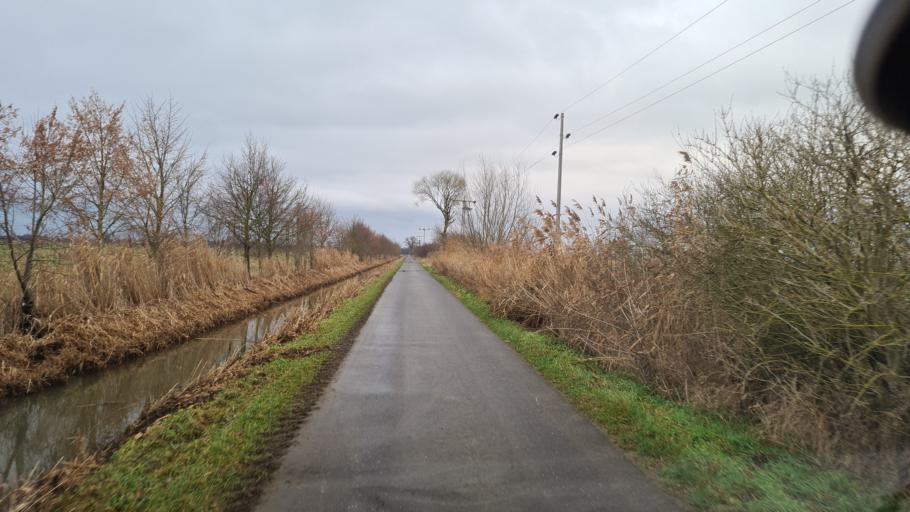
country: DE
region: Brandenburg
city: Ziltendorf
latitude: 52.2409
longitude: 14.6624
